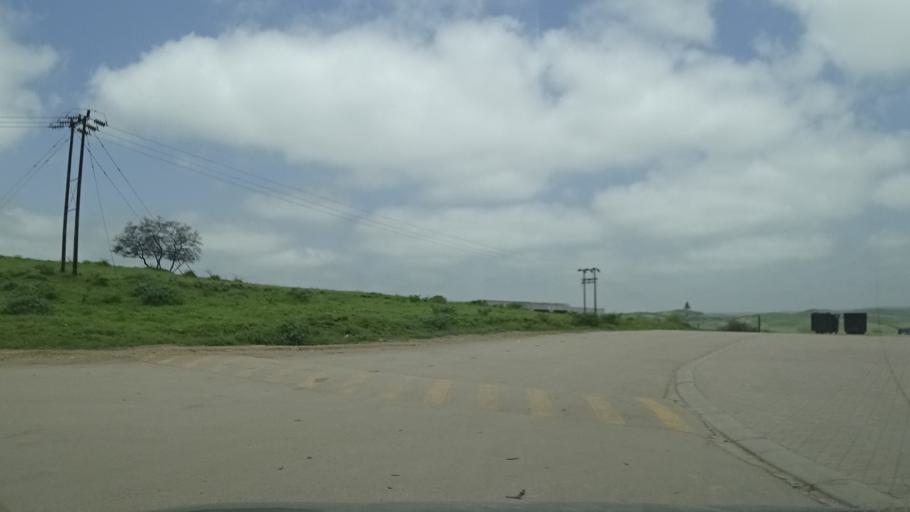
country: OM
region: Zufar
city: Salalah
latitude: 17.1923
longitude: 54.1652
